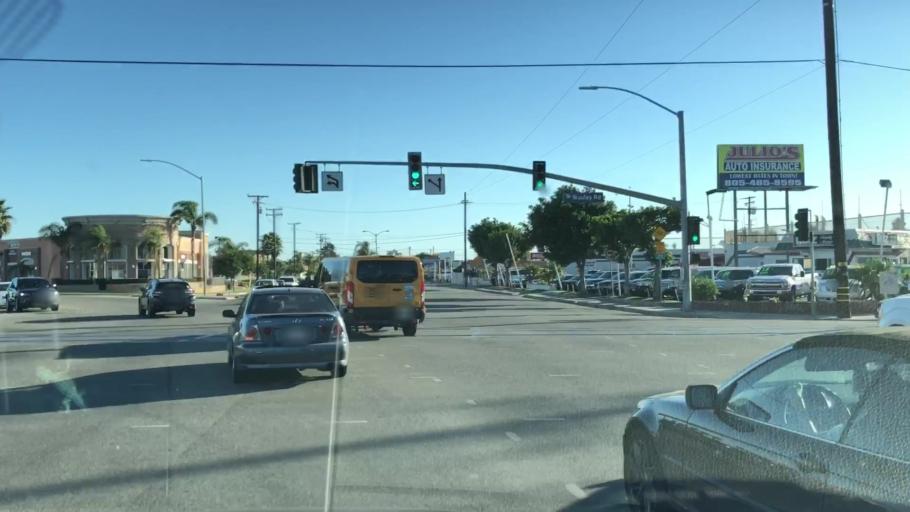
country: US
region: California
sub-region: Ventura County
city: Oxnard
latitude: 34.1901
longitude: -119.1774
